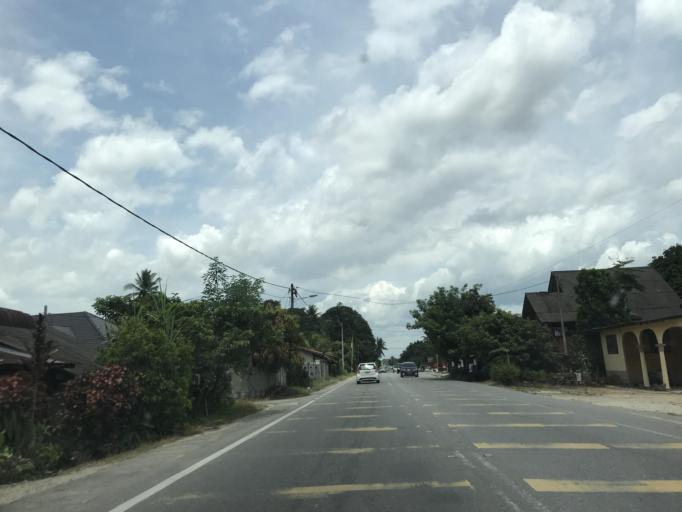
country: MY
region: Kelantan
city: Kota Bharu
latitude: 6.0748
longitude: 102.2085
